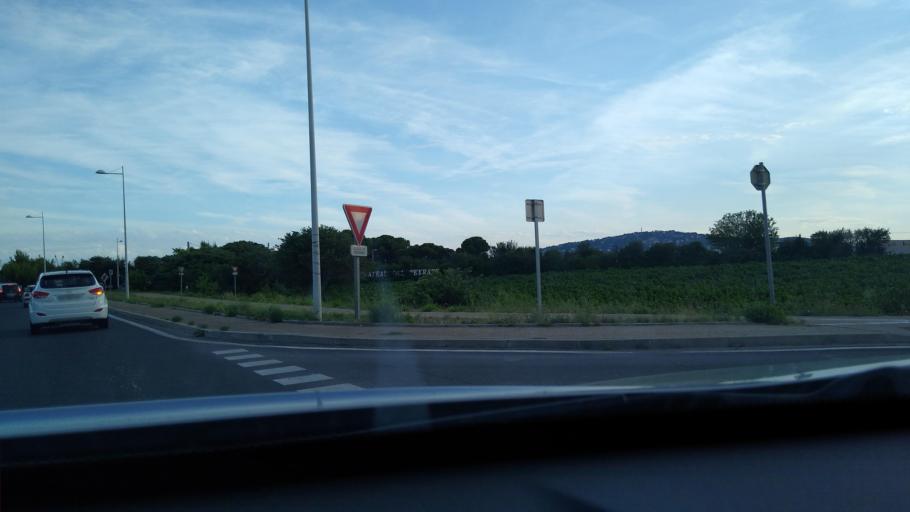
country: FR
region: Languedoc-Roussillon
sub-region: Departement de l'Herault
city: Sete
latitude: 43.4241
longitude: 3.7226
